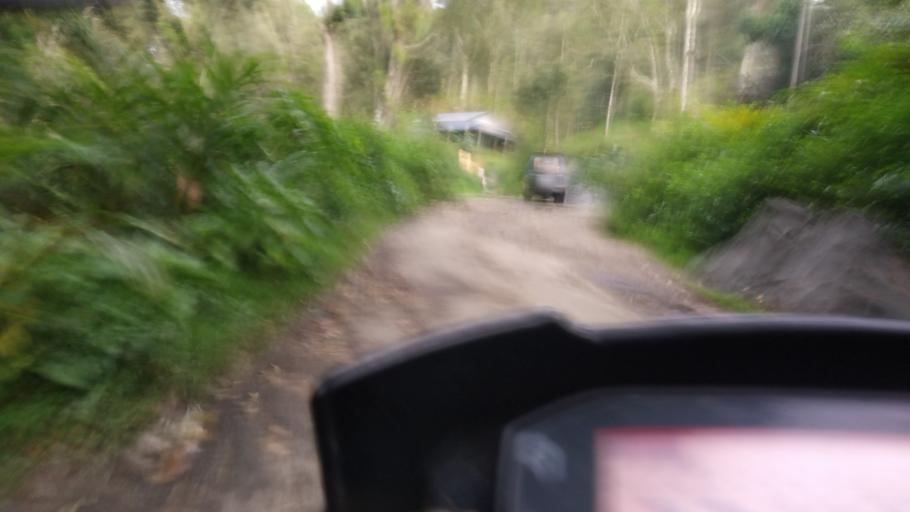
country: IN
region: Tamil Nadu
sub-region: Theni
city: Bodinayakkanur
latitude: 10.0233
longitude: 77.2487
